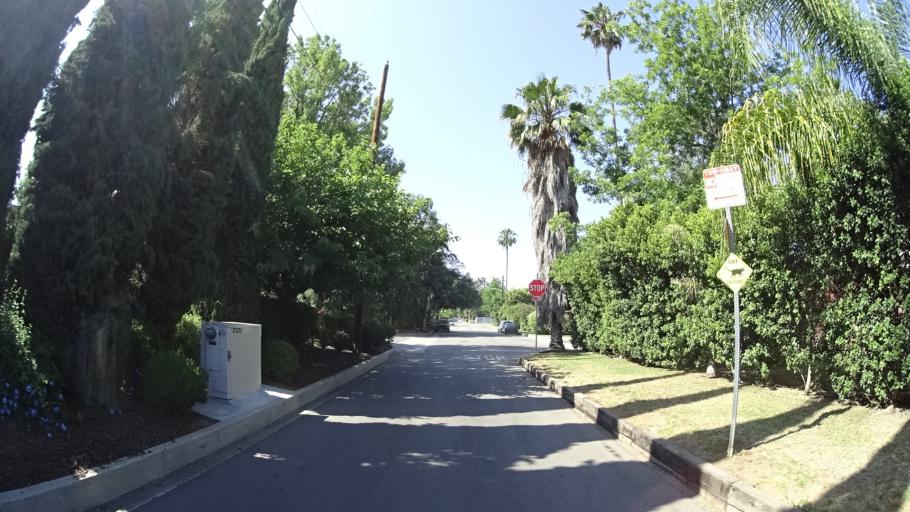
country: US
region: California
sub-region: Los Angeles County
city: Sherman Oaks
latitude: 34.1618
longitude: -118.4531
